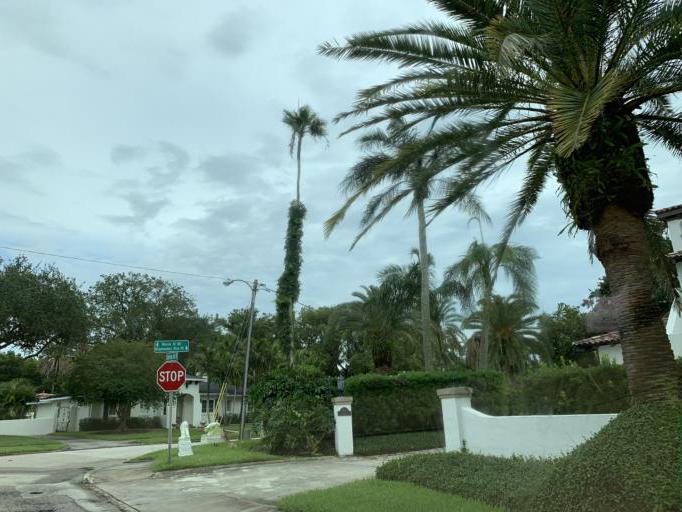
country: US
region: Florida
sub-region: Pinellas County
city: Saint Petersburg
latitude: 27.7922
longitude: -82.6225
